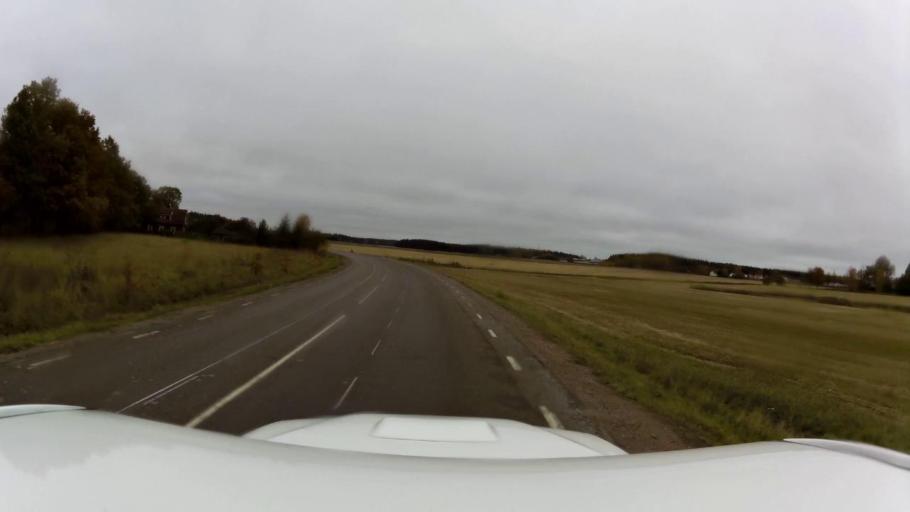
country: SE
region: OEstergoetland
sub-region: Linkopings Kommun
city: Linghem
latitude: 58.4382
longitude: 15.7147
